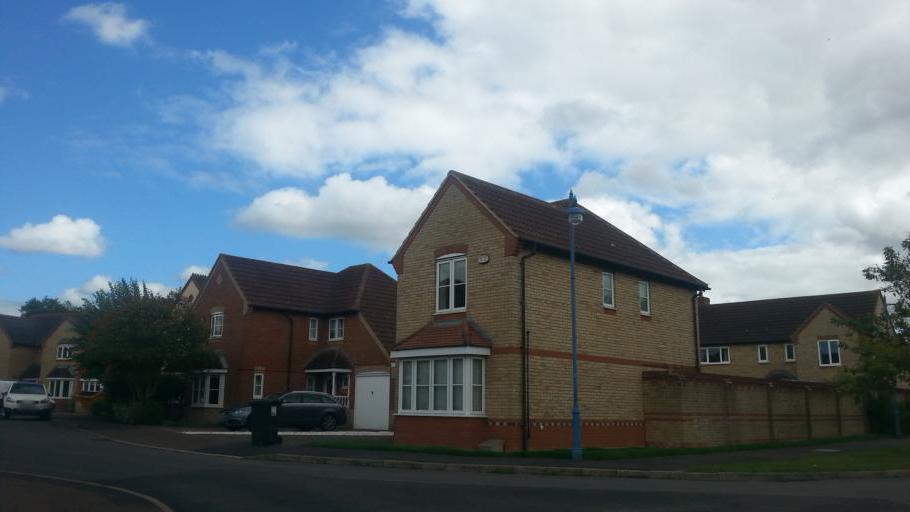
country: GB
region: England
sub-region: Cambridgeshire
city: Papworth Everard
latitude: 52.2153
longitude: -0.0725
